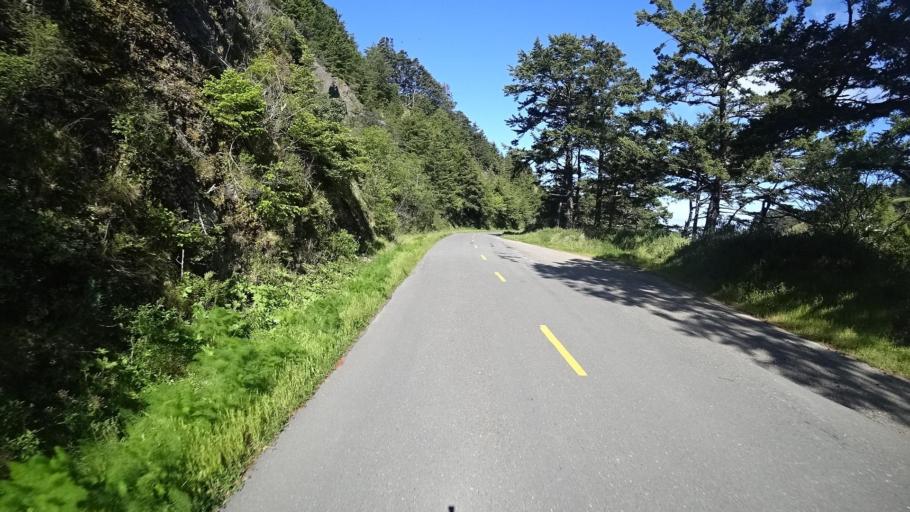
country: US
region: California
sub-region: Humboldt County
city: Ferndale
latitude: 40.3481
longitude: -124.3539
